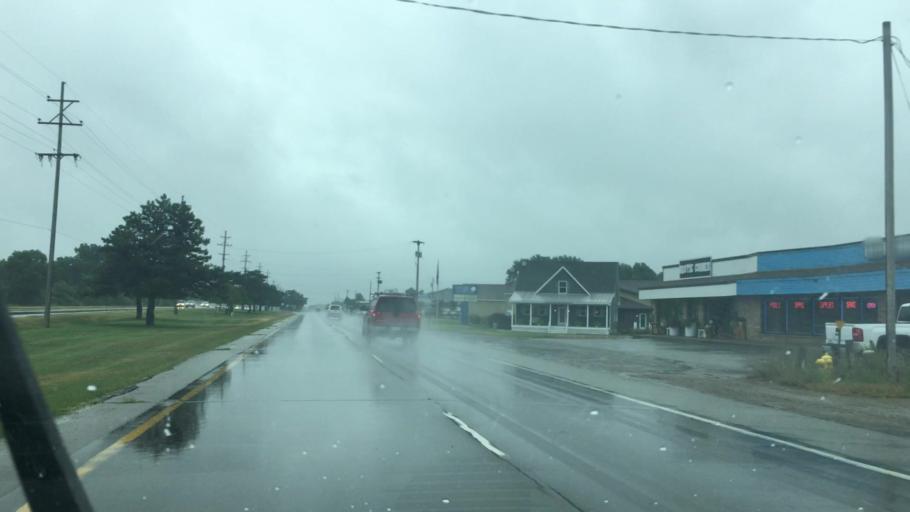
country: US
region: Michigan
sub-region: Ottawa County
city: Jenison
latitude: 42.8976
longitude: -85.8065
